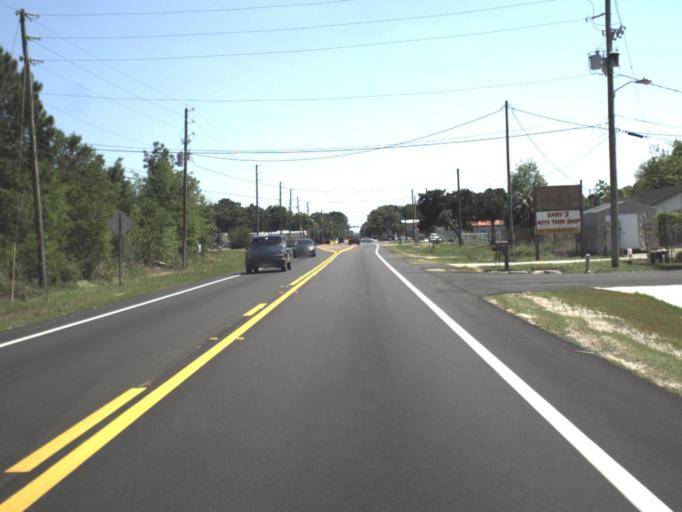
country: US
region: Florida
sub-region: Bay County
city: Cedar Grove
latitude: 30.1780
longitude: -85.6078
